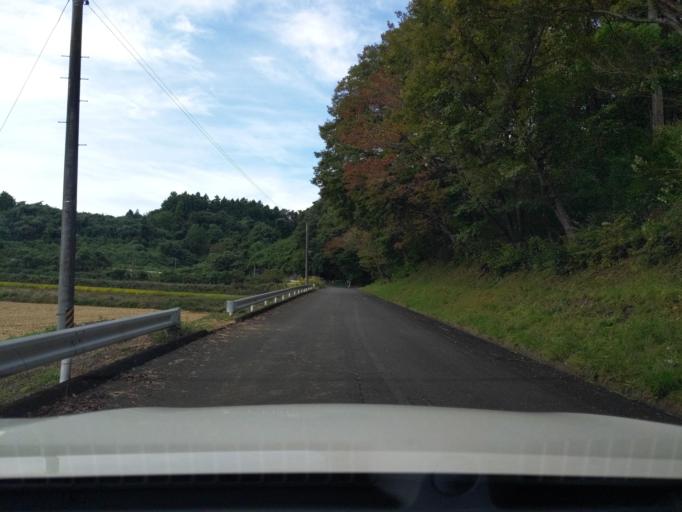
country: JP
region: Fukushima
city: Koriyama
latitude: 37.4109
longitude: 140.2776
